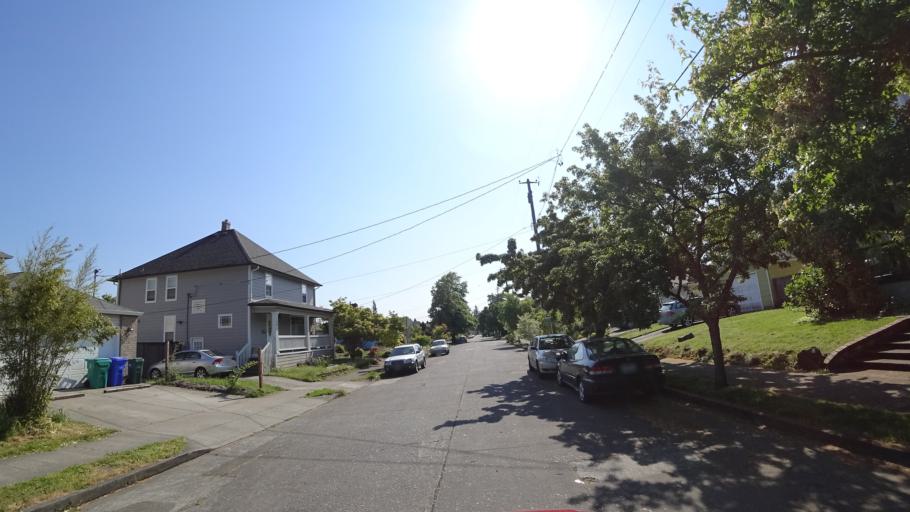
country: US
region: Oregon
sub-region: Multnomah County
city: Portland
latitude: 45.5684
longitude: -122.6499
